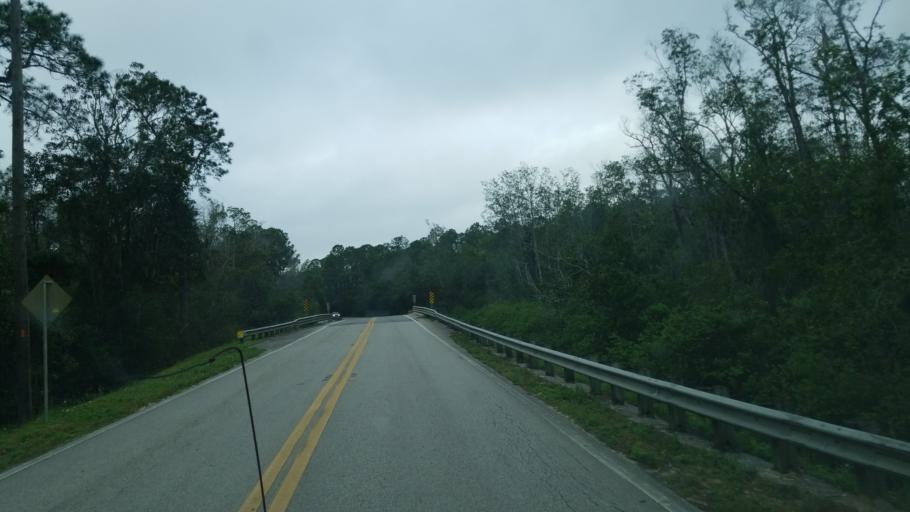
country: US
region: Florida
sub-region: Lake County
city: Four Corners
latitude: 28.2591
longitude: -81.7302
